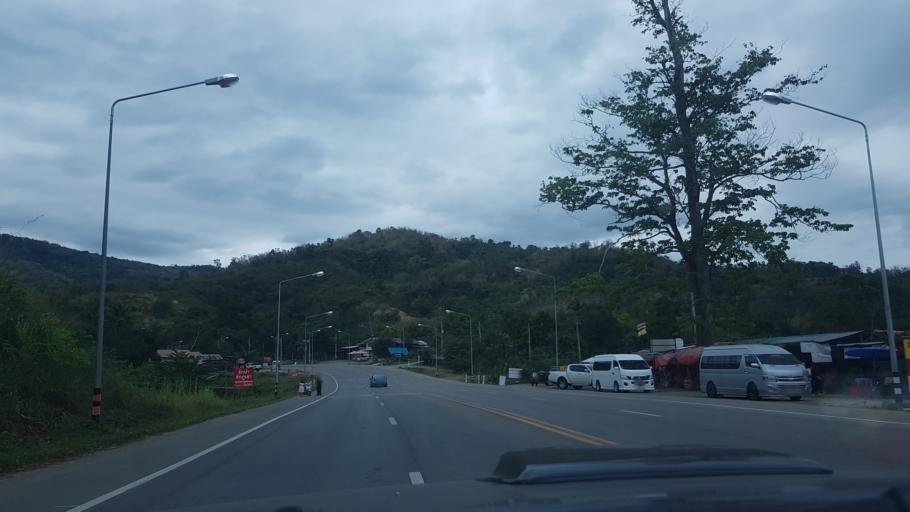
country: TH
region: Phetchabun
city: Khao Kho
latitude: 16.5430
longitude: 101.0542
